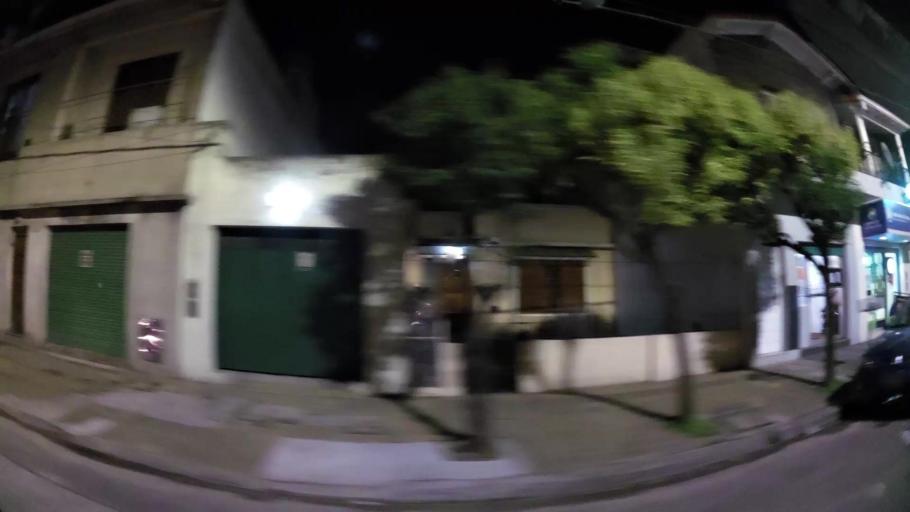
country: AR
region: Buenos Aires
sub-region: Partido de Lanus
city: Lanus
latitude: -34.7137
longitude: -58.3527
